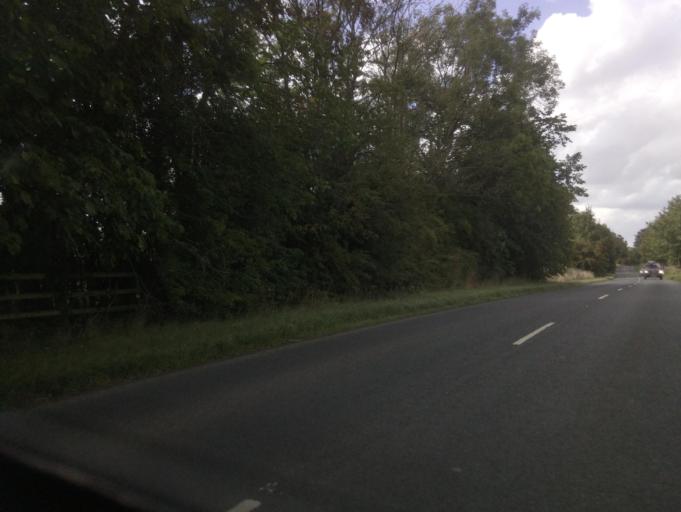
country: GB
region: England
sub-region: North Yorkshire
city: Ripon
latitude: 54.1964
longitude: -1.5774
